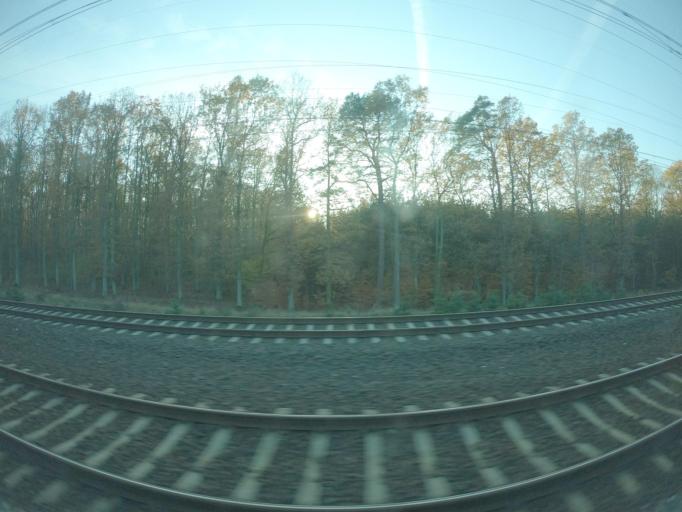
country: PL
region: Lubusz
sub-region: Powiat slubicki
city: Rzepin
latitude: 52.3213
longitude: 14.8499
